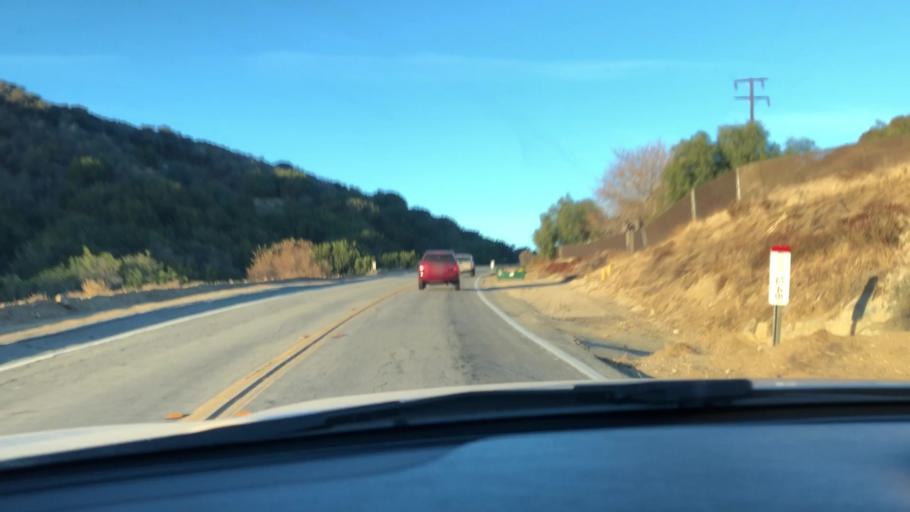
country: US
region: California
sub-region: Los Angeles County
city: Green Valley
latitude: 34.6590
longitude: -118.3519
